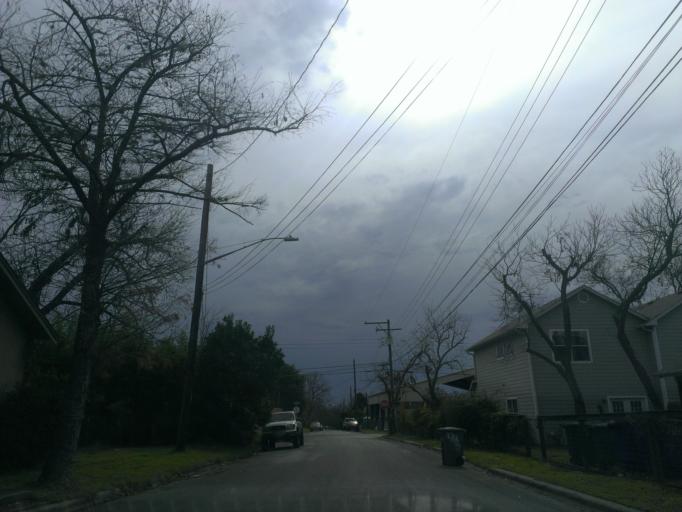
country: US
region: Texas
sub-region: Travis County
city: Austin
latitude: 30.2837
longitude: -97.7201
